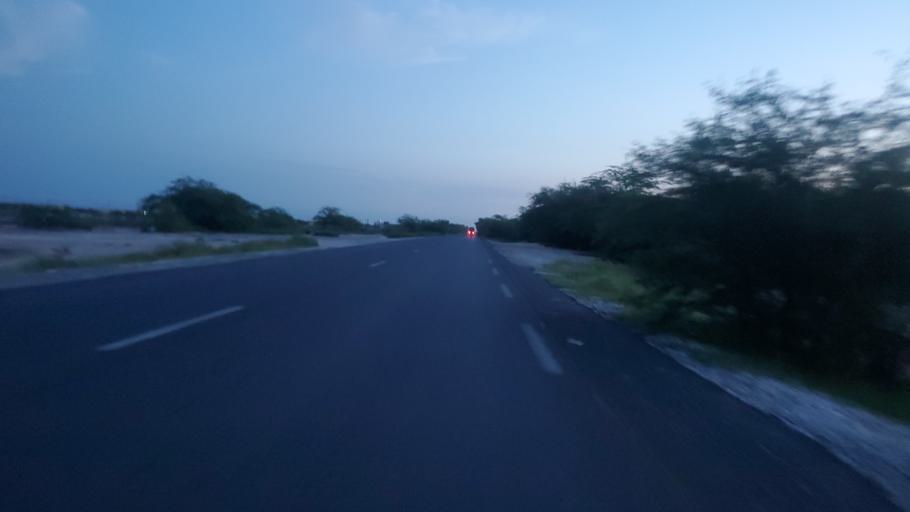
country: SN
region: Saint-Louis
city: Saint-Louis
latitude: 16.0648
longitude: -16.3937
